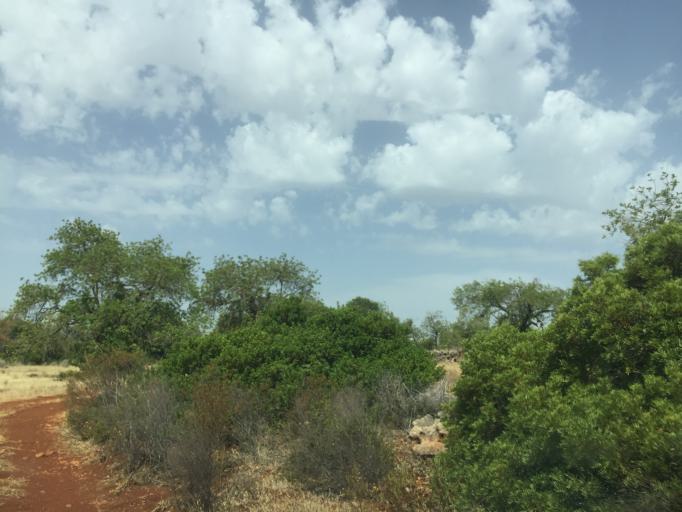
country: PT
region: Faro
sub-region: Loule
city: Boliqueime
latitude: 37.1339
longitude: -8.1359
